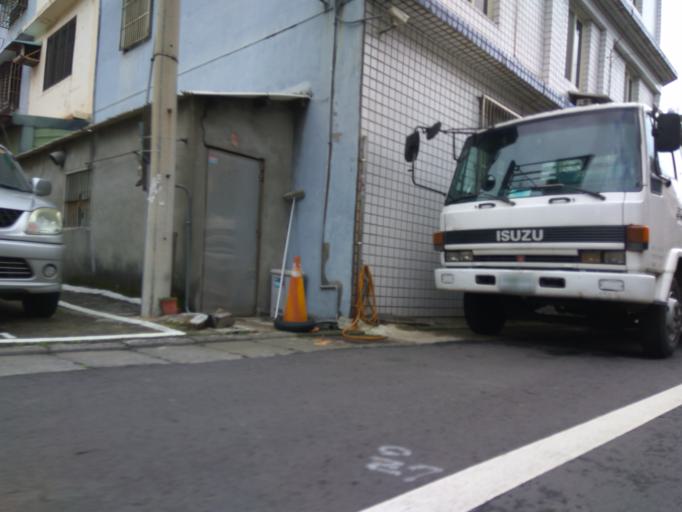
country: TW
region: Taiwan
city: Taoyuan City
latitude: 24.9598
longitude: 121.2038
